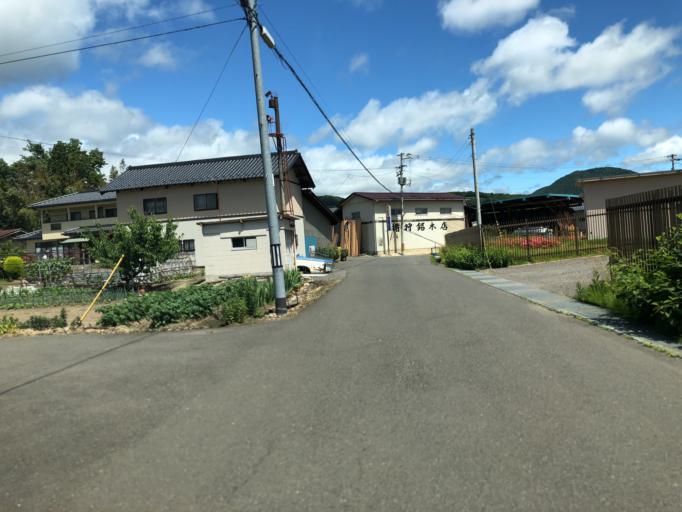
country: JP
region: Fukushima
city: Fukushima-shi
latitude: 37.8190
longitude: 140.4237
